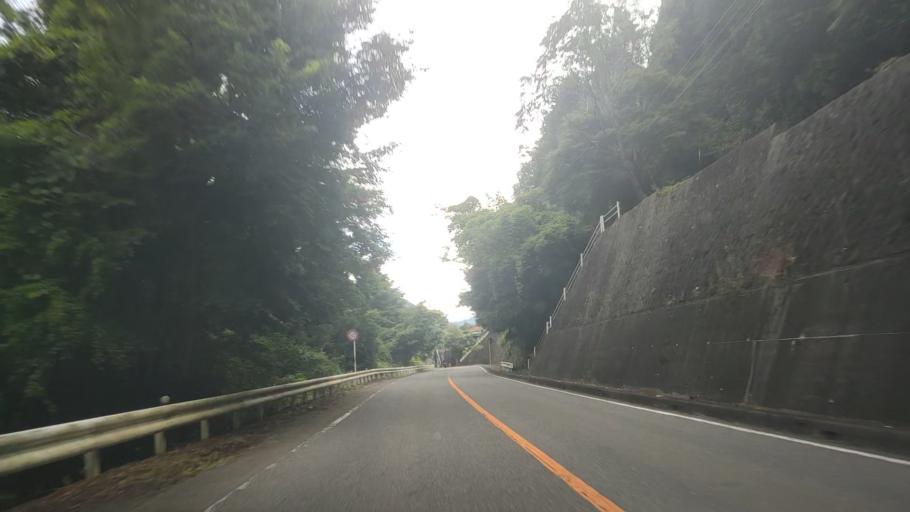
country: JP
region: Gunma
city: Kiryu
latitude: 36.5832
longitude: 139.3964
